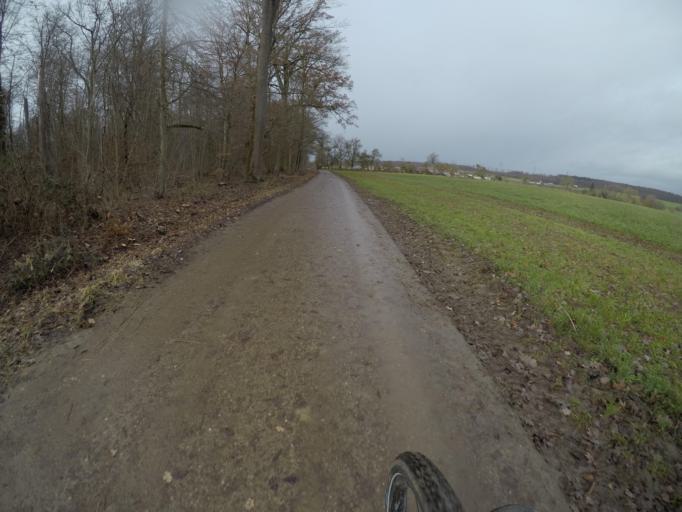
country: DE
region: Baden-Wuerttemberg
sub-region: Regierungsbezirk Stuttgart
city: Hemmingen
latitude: 48.8594
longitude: 9.0156
